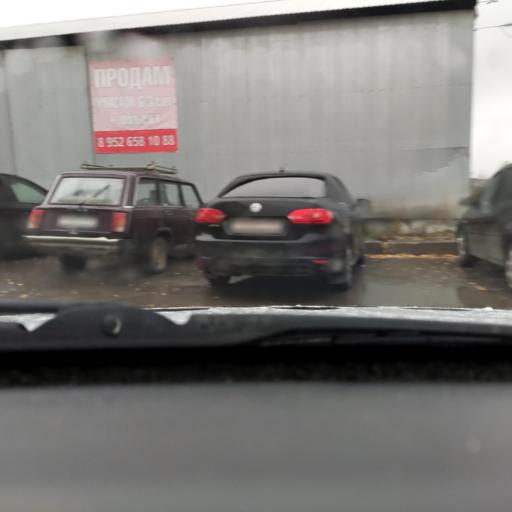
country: RU
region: Perm
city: Perm
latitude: 58.0238
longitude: 56.2716
